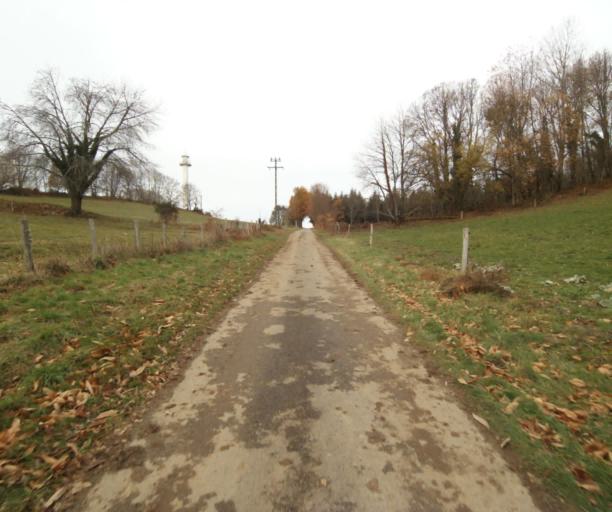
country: FR
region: Limousin
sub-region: Departement de la Correze
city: Sainte-Fortunade
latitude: 45.1912
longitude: 1.7682
